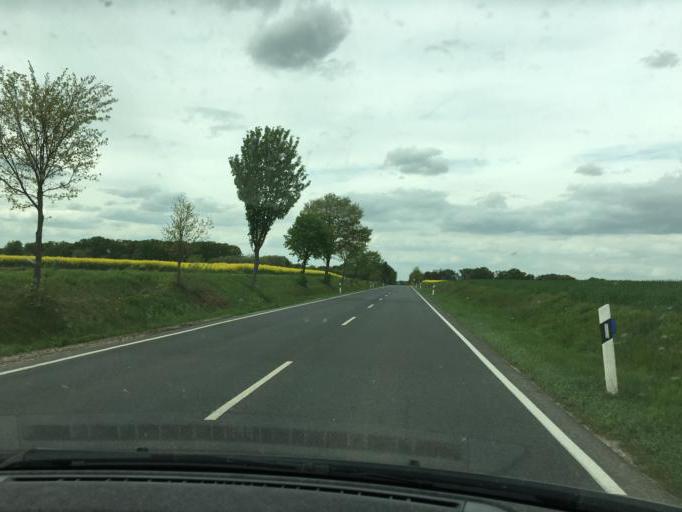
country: DE
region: North Rhine-Westphalia
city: Zulpich
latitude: 50.7256
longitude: 6.6792
